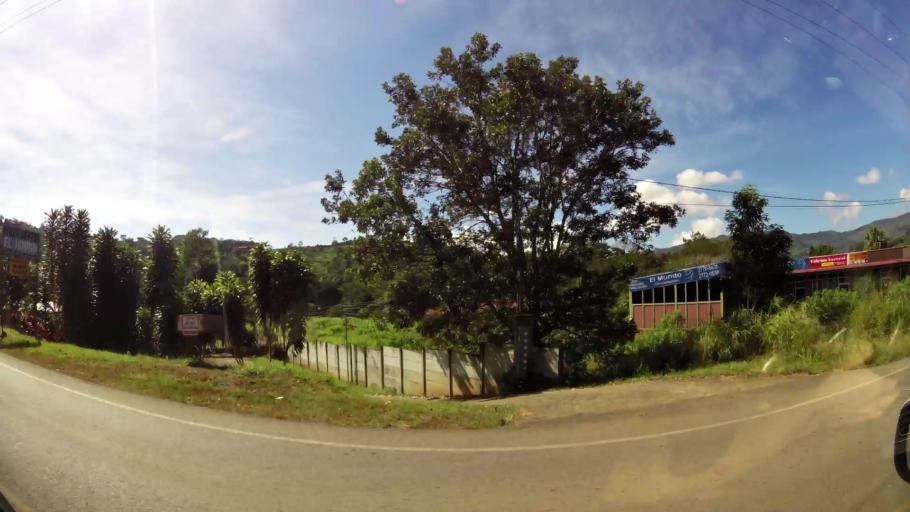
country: CR
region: San Jose
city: San Isidro
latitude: 9.3611
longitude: -83.7130
